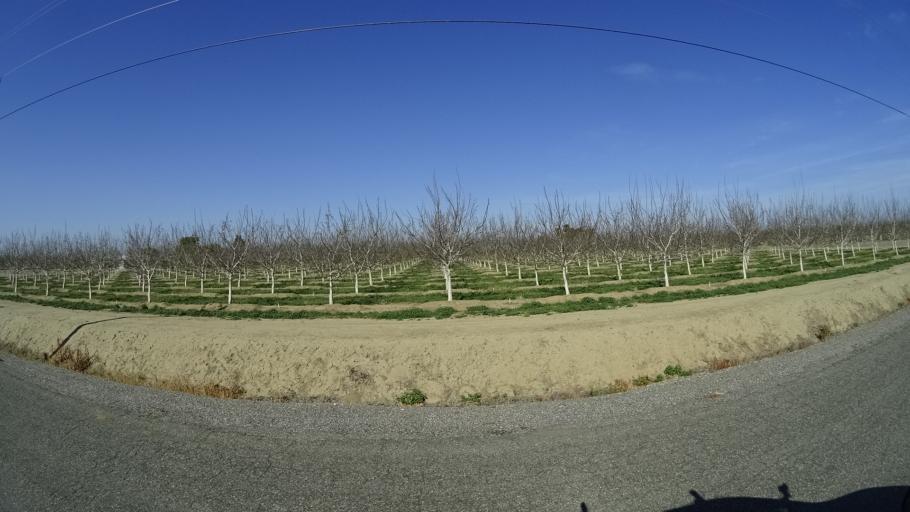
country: US
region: California
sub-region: Glenn County
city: Willows
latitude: 39.5740
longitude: -122.1170
